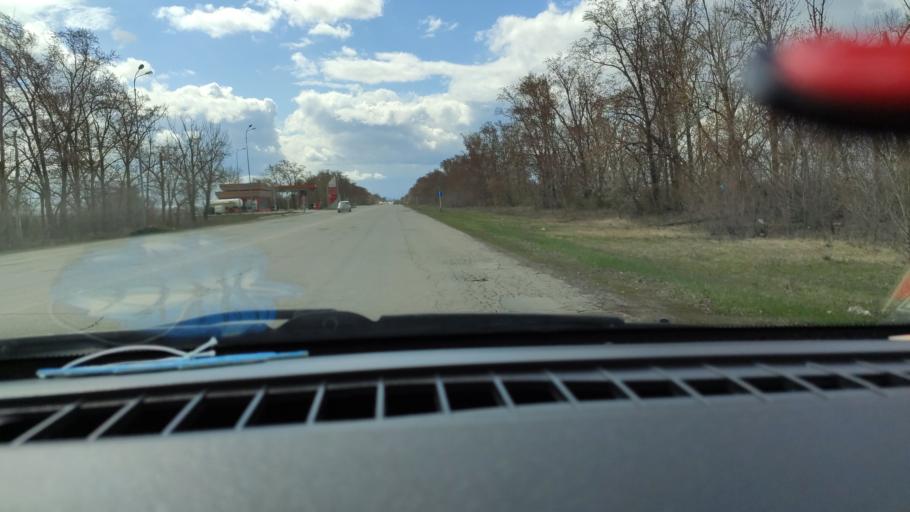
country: RU
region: Samara
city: Tol'yatti
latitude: 53.5925
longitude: 49.4067
